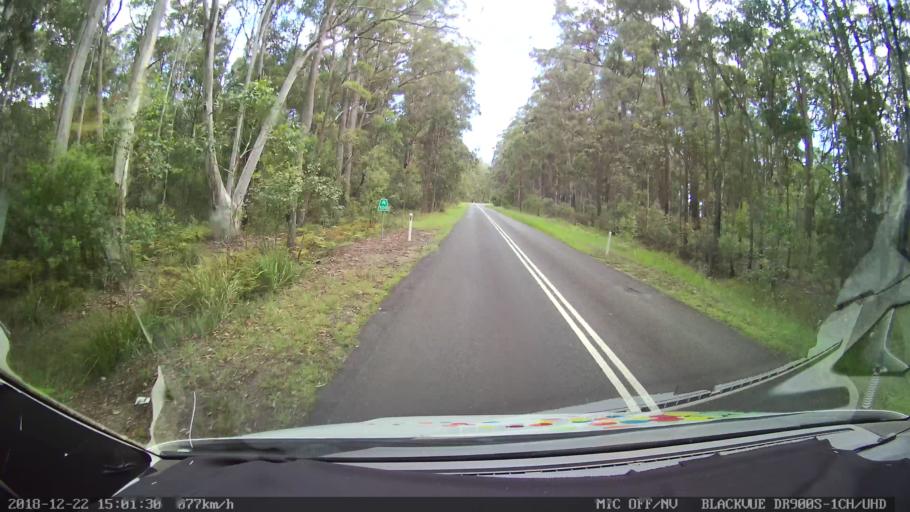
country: AU
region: New South Wales
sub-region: Bellingen
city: Dorrigo
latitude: -30.2551
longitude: 152.4584
